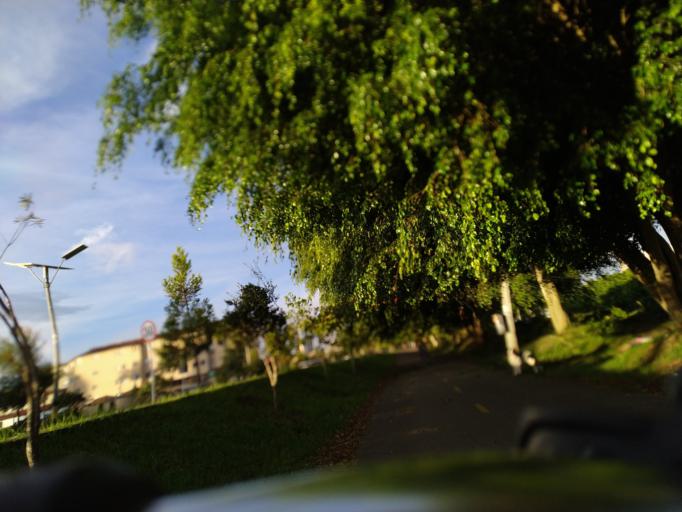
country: CO
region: Antioquia
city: Rionegro
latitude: 6.1488
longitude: -75.3738
